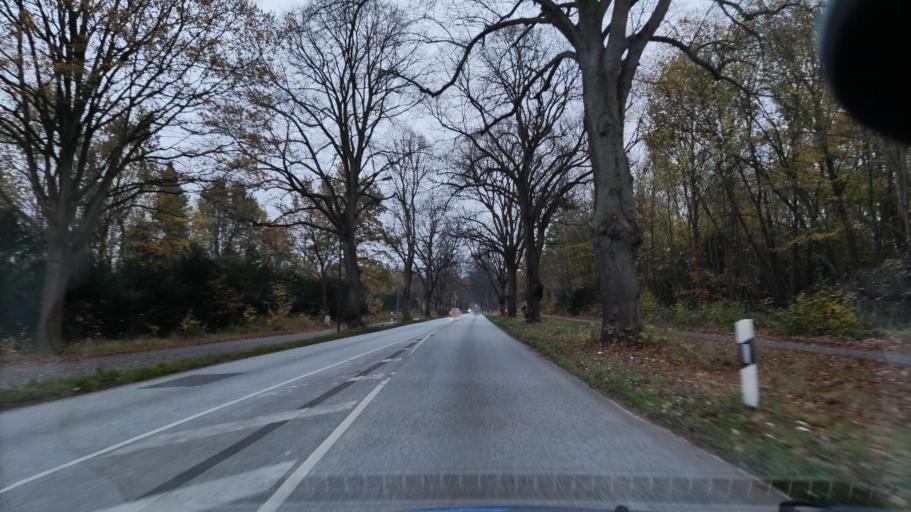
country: DE
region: Schleswig-Holstein
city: Gross Gronau
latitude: 53.8304
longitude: 10.7178
